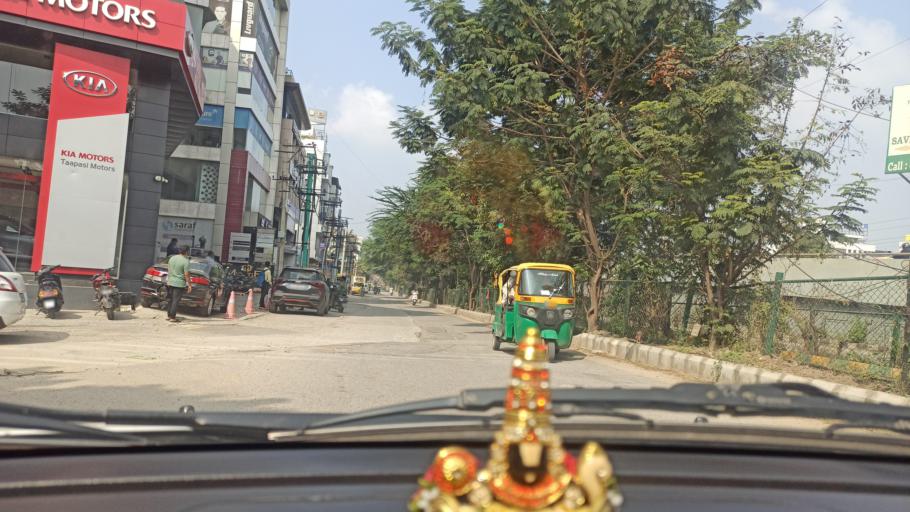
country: IN
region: Karnataka
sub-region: Bangalore Urban
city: Bangalore
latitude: 13.0229
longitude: 77.6454
